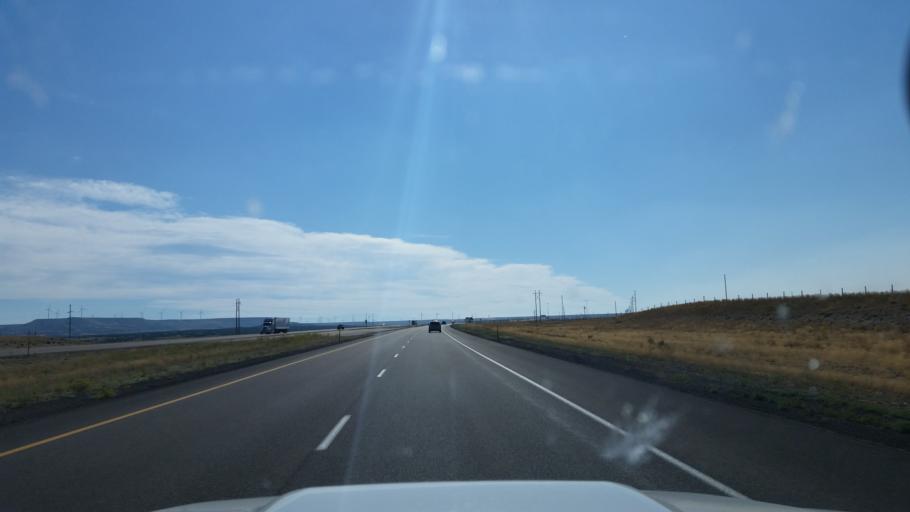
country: US
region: Wyoming
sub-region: Uinta County
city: Mountain View
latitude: 41.3348
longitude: -110.4164
